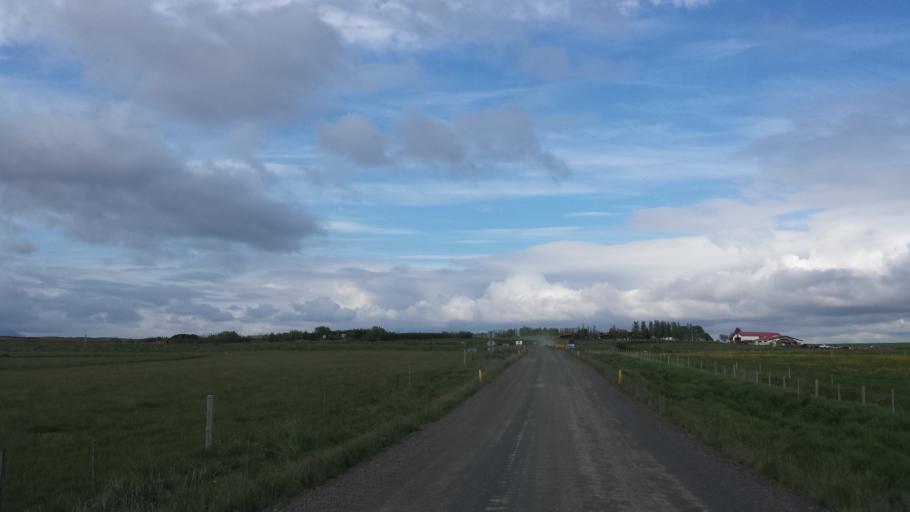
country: IS
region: South
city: Selfoss
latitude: 64.3080
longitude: -20.2346
